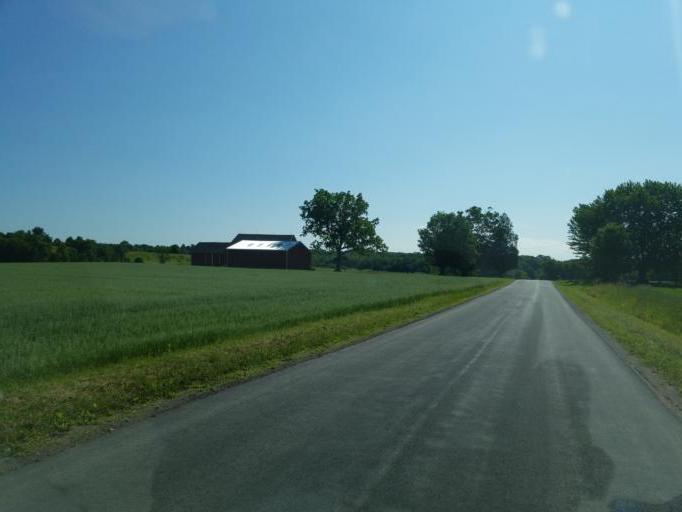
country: US
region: New York
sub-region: Wayne County
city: Clyde
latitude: 43.0550
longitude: -76.8836
